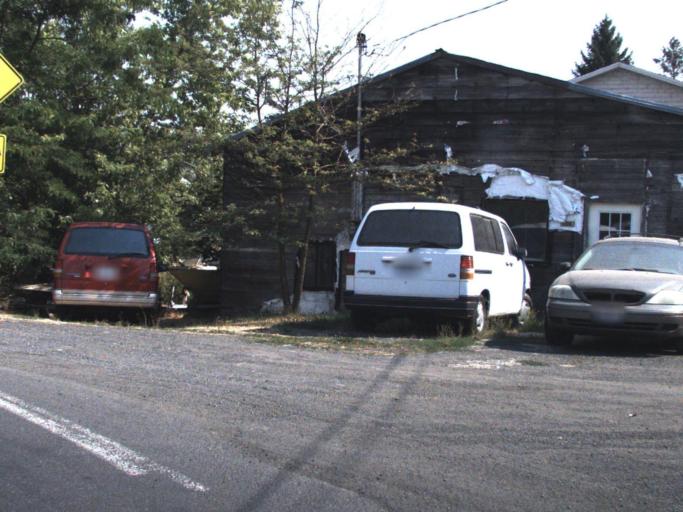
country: US
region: Idaho
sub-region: Latah County
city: Moscow
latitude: 46.9089
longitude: -117.0766
